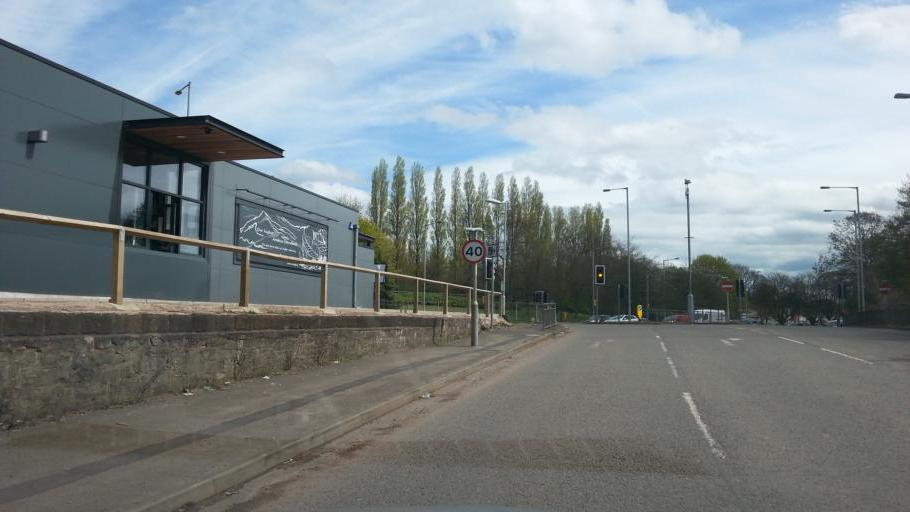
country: GB
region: England
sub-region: Staffordshire
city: Newcastle under Lyme
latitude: 53.0325
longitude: -2.2398
